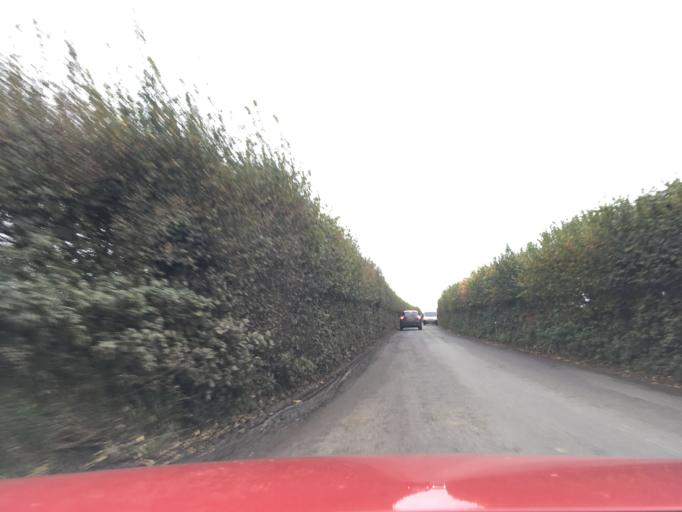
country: GB
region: England
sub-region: Somerset
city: South Petherton
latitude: 50.9344
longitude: -2.8285
